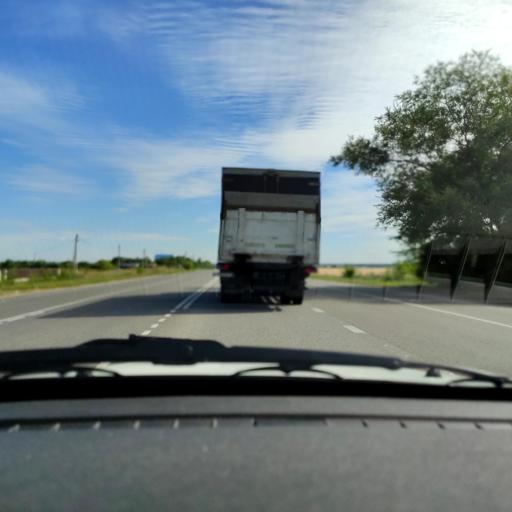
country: RU
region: Voronezj
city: Orlovo
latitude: 51.7357
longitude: 39.5655
